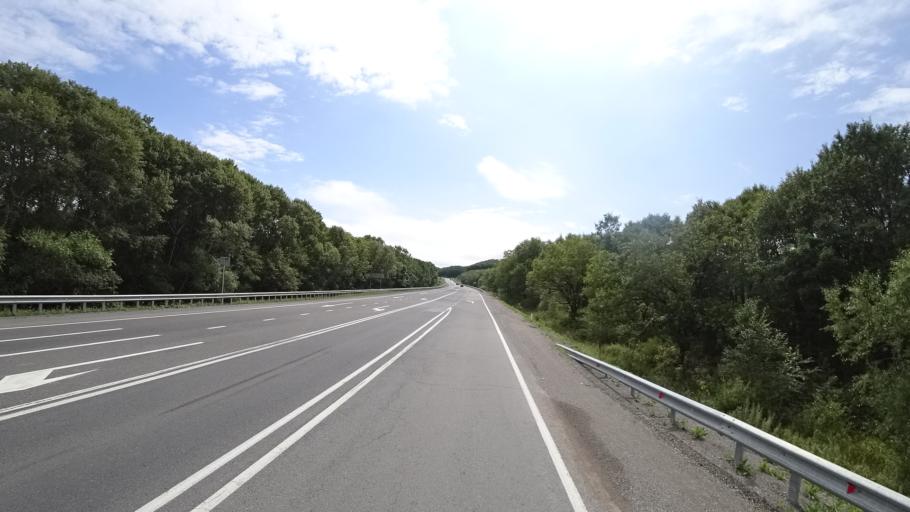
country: RU
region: Primorskiy
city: Lyalichi
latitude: 44.1389
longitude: 132.4289
